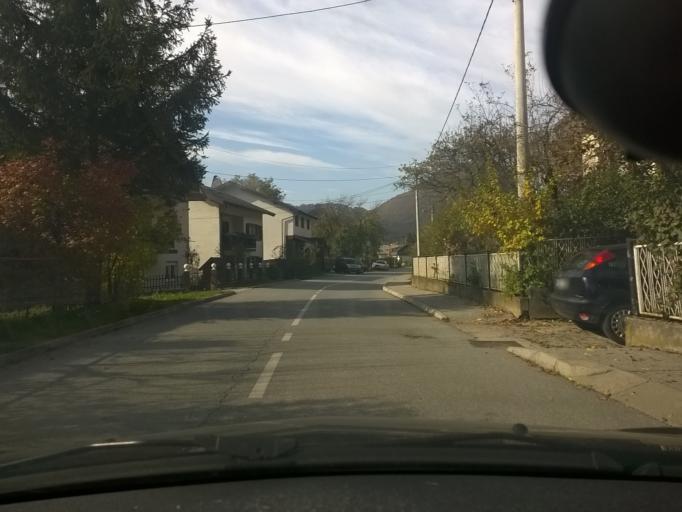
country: HR
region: Krapinsko-Zagorska
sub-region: Grad Krapina
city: Krapina
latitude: 46.1807
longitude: 15.8663
